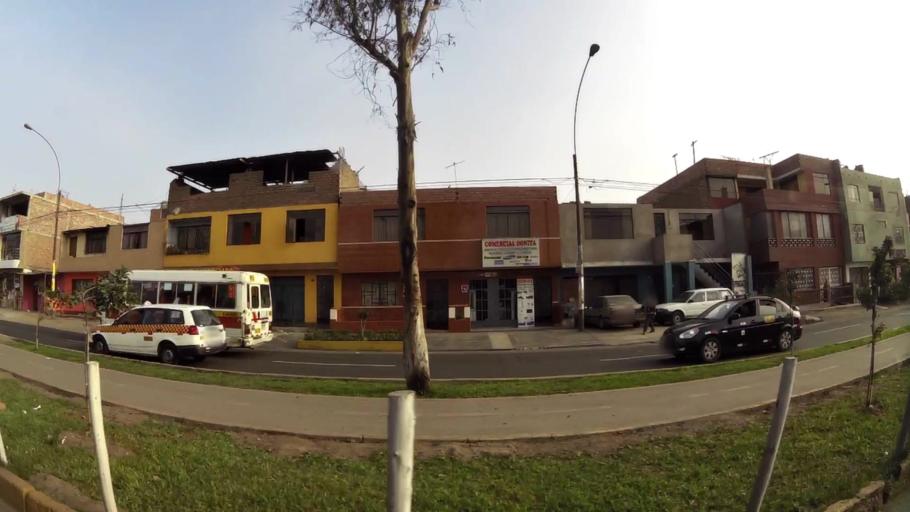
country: PE
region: Lima
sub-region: Lima
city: Independencia
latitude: -12.0234
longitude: -77.0817
